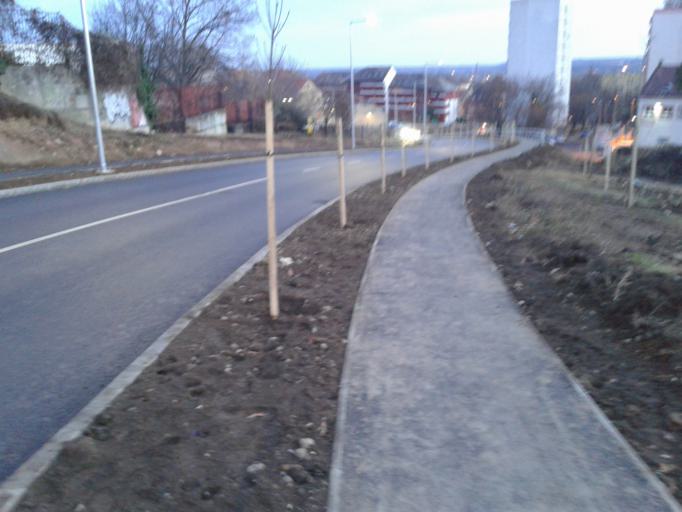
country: HU
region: Baranya
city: Pecs
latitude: 46.0780
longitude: 18.2137
